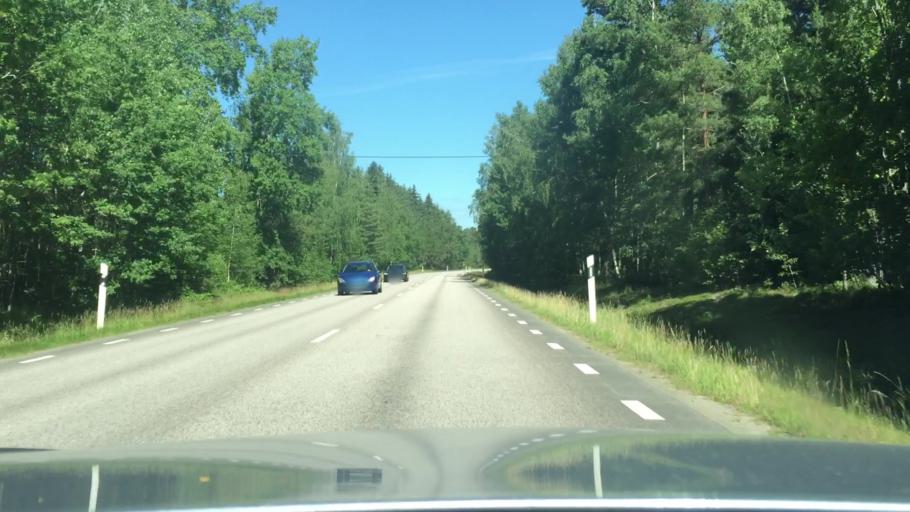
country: SE
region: Vaestra Goetaland
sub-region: Mariestads Kommun
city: Mariestad
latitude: 58.6759
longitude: 13.8504
